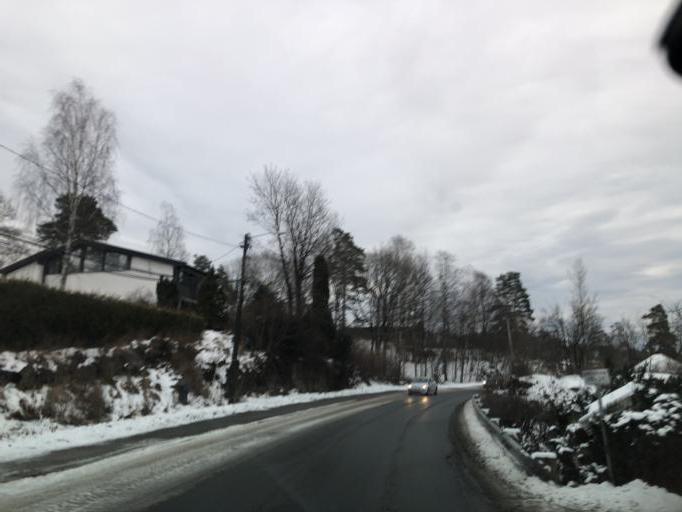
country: NO
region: Akershus
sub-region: Baerum
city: Sandvika
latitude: 59.8737
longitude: 10.5090
